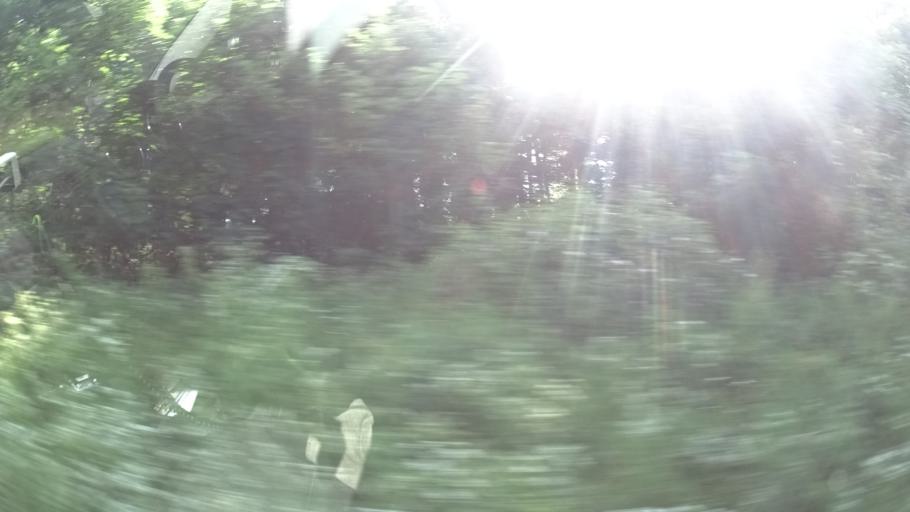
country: DE
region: Hesse
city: Rosenthal
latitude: 50.9327
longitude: 8.8393
